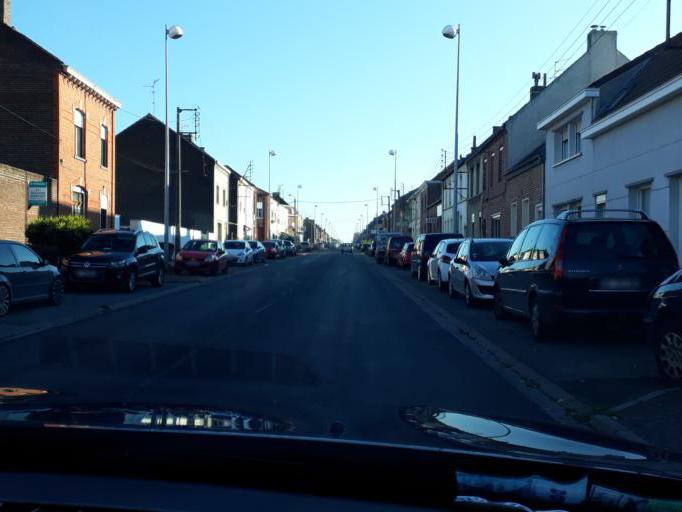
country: FR
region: Nord-Pas-de-Calais
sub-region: Departement du Nord
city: Aniche
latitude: 50.3276
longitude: 3.2467
